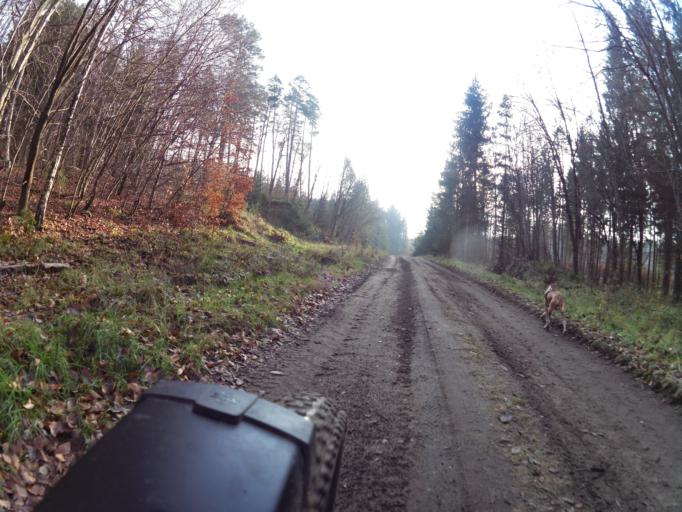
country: PL
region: West Pomeranian Voivodeship
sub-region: Powiat koszalinski
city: Polanow
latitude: 54.1869
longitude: 16.7183
